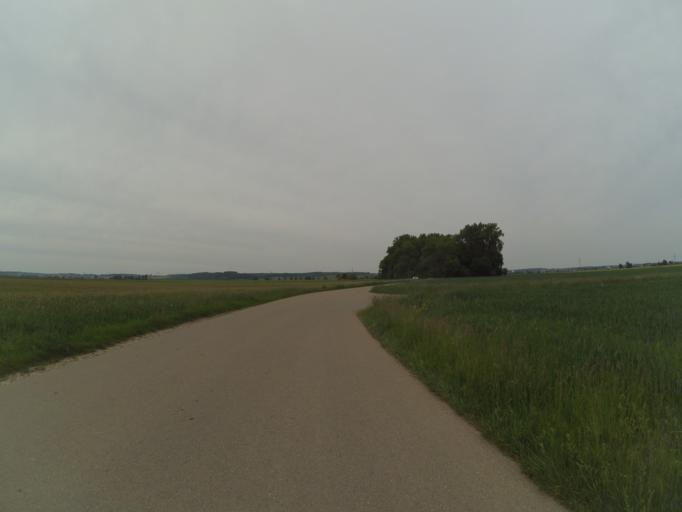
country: DE
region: Baden-Wuerttemberg
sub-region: Regierungsbezirk Stuttgart
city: Sontheim an der Brenz
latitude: 48.5277
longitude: 10.2882
